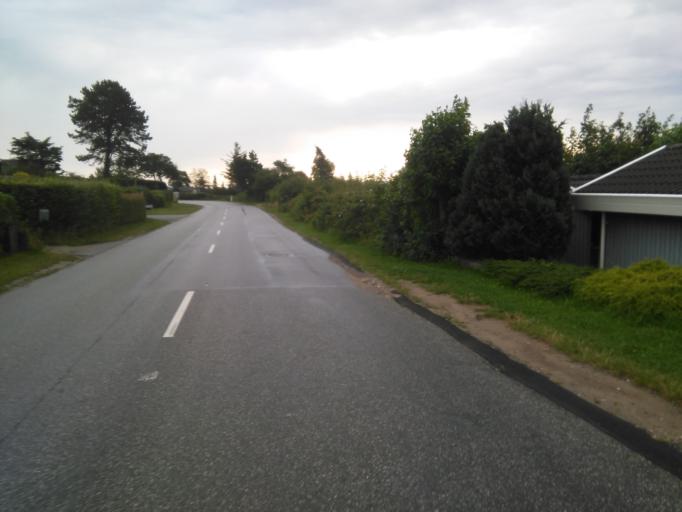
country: DK
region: Central Jutland
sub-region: Arhus Kommune
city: Logten
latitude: 56.2305
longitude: 10.3229
